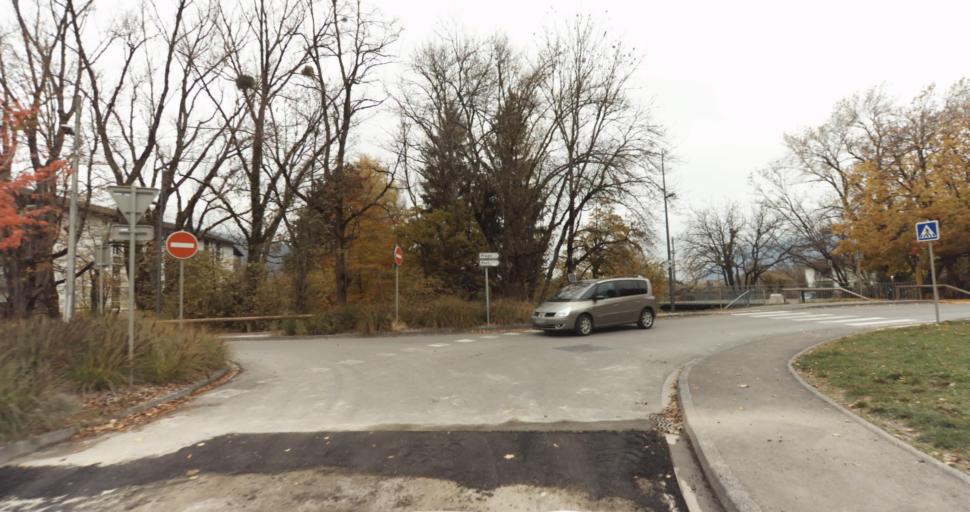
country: FR
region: Rhone-Alpes
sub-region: Departement de la Haute-Savoie
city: Saint-Jorioz
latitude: 45.8348
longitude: 6.1658
